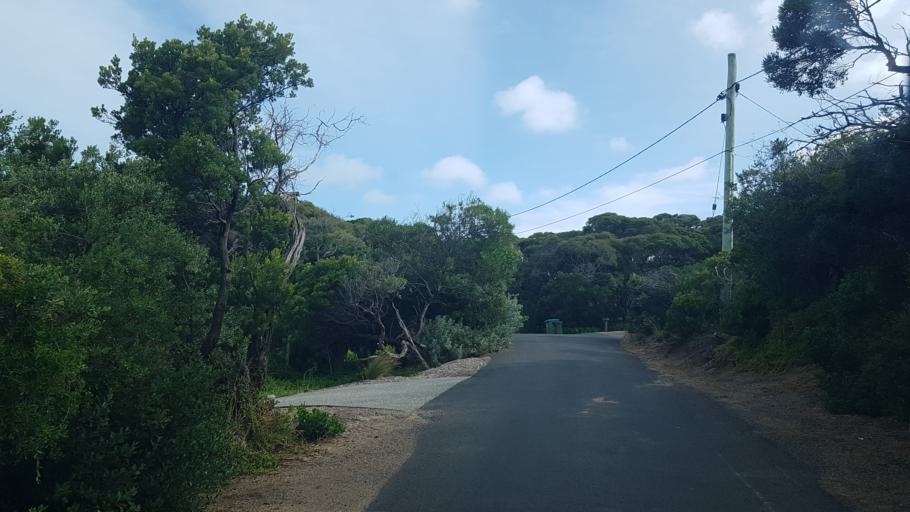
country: AU
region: Victoria
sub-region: Mornington Peninsula
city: Sorrento
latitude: -38.3283
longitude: 144.7076
